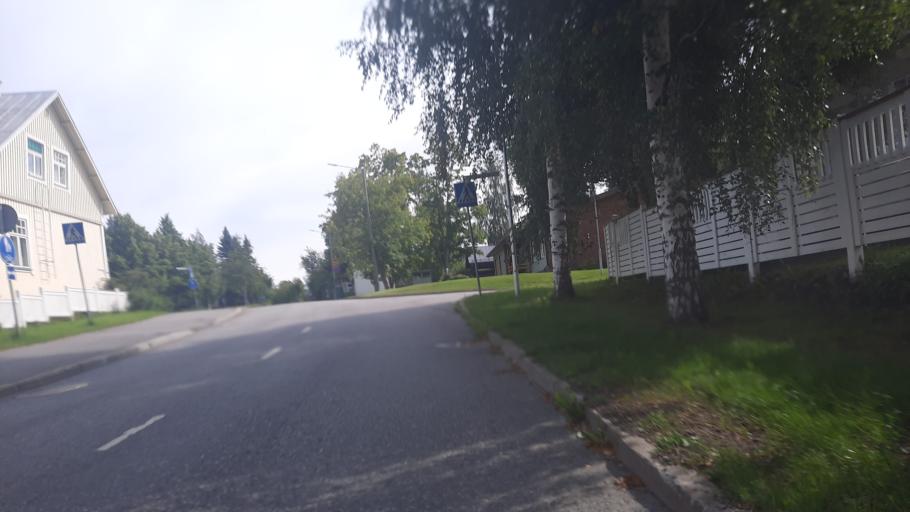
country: FI
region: North Karelia
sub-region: Joensuu
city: Joensuu
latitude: 62.5968
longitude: 29.7861
